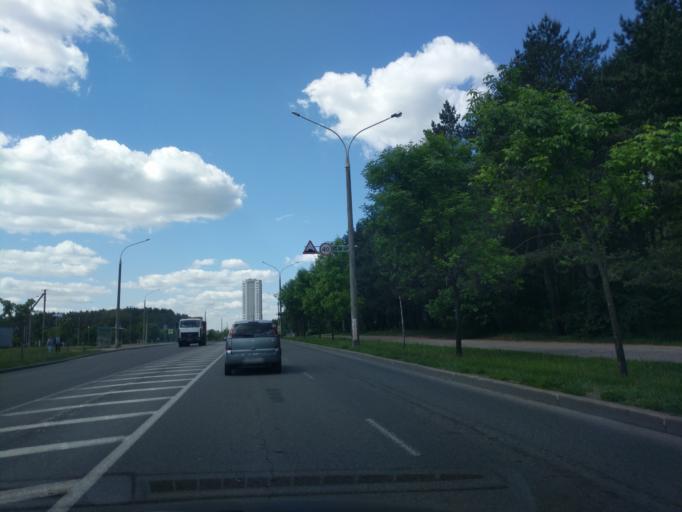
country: BY
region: Minsk
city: Borovlyany
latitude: 53.9256
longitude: 27.6634
